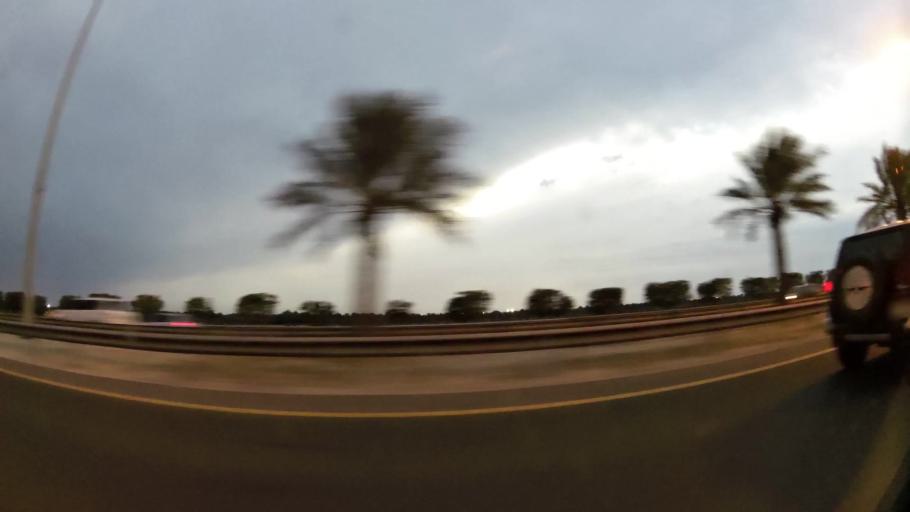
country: BH
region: Central Governorate
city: Madinat Hamad
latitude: 26.1587
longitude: 50.5054
